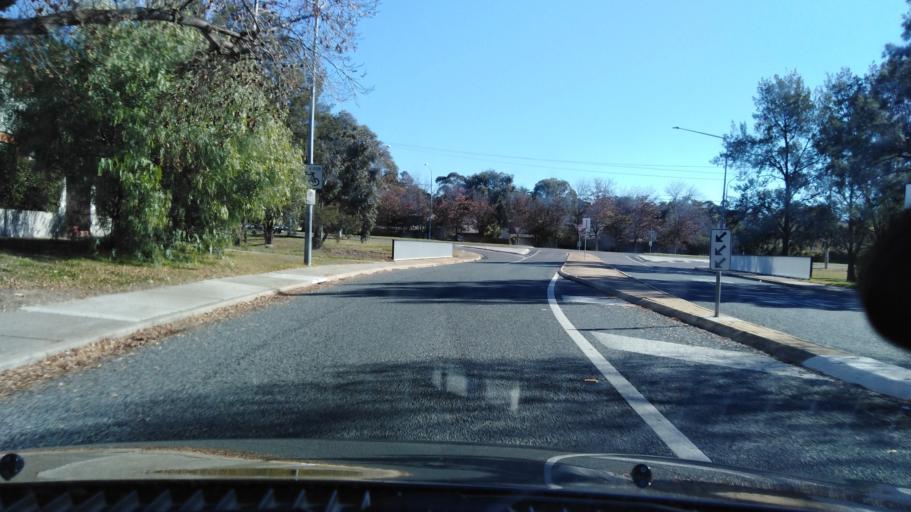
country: AU
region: Australian Capital Territory
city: Forrest
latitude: -35.3393
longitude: 149.0522
